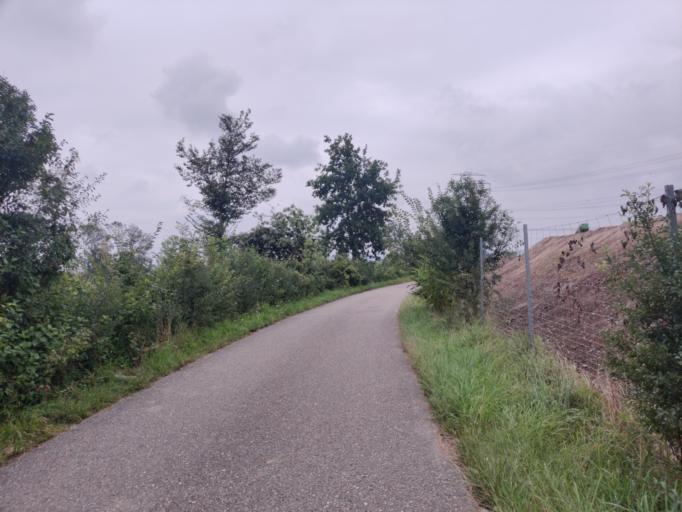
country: AT
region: Lower Austria
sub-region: Politischer Bezirk Tulln
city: Michelhausen
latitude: 48.3315
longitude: 15.9593
